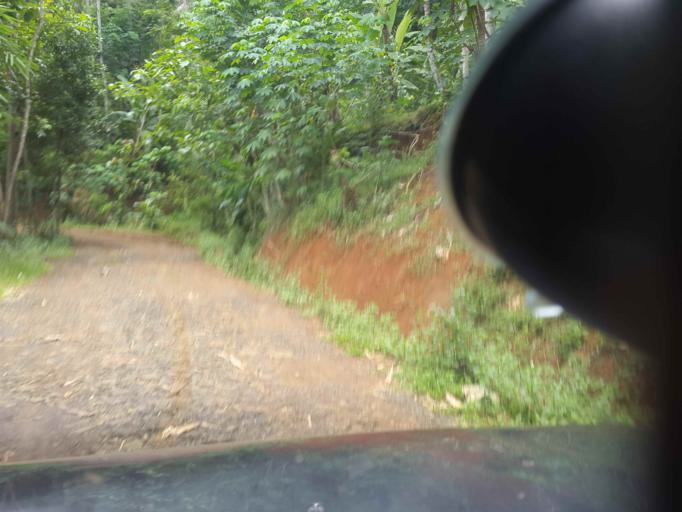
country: ID
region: Central Java
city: Binangun
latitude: -7.5535
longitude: 109.2603
